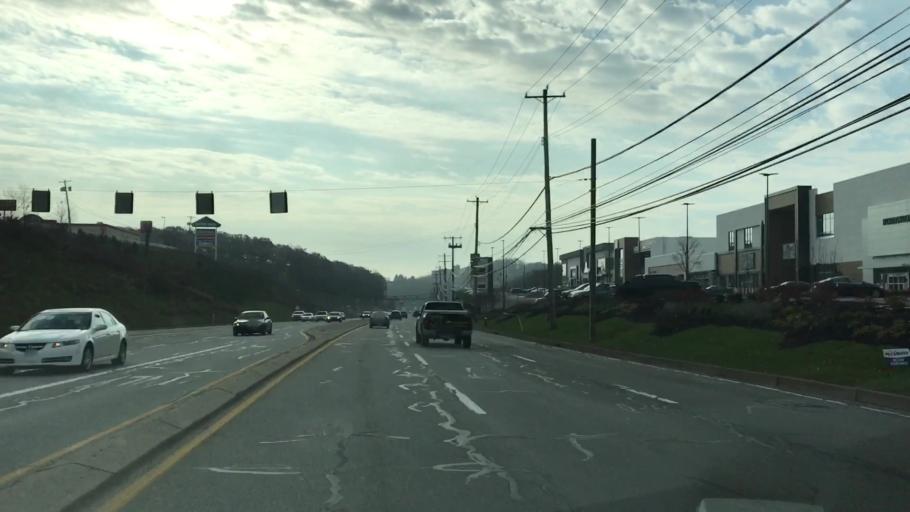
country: US
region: Pennsylvania
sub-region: Allegheny County
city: West View
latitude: 40.5532
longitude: -80.0206
